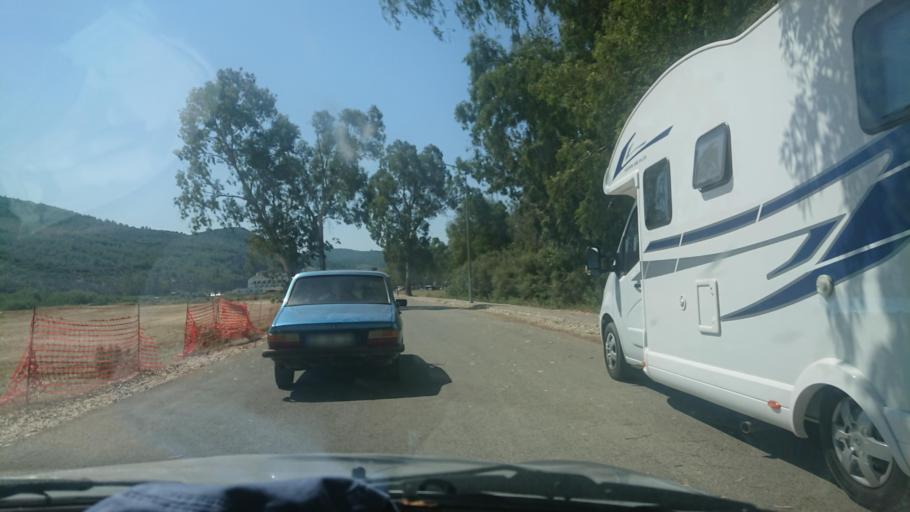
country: TR
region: Aydin
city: Kusadasi
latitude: 37.9400
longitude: 27.2771
